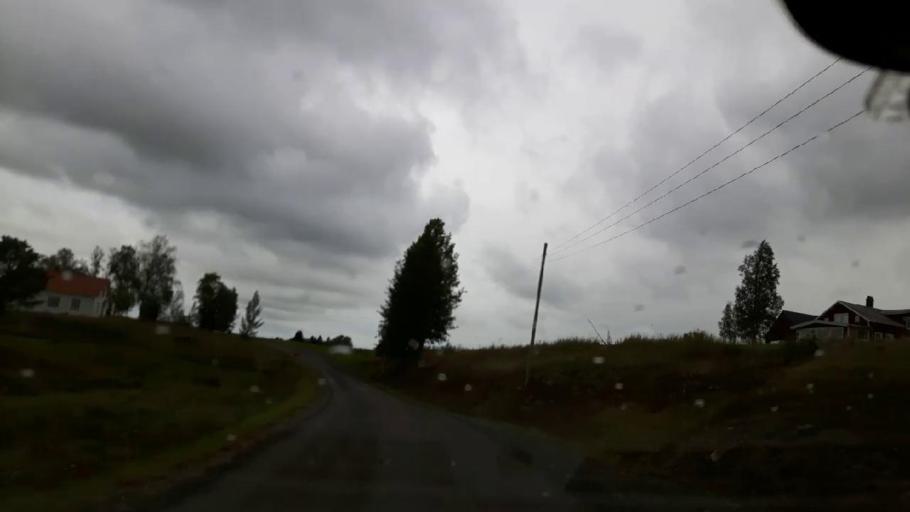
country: SE
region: Jaemtland
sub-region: OEstersunds Kommun
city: Ostersund
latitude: 63.0298
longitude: 14.5829
